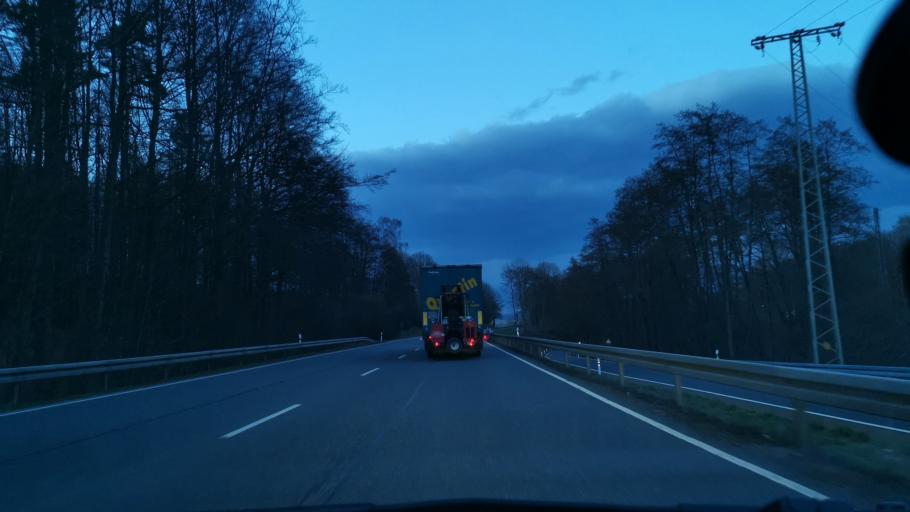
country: DE
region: Hesse
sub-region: Regierungsbezirk Kassel
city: Cornberg
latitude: 51.0327
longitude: 9.8578
